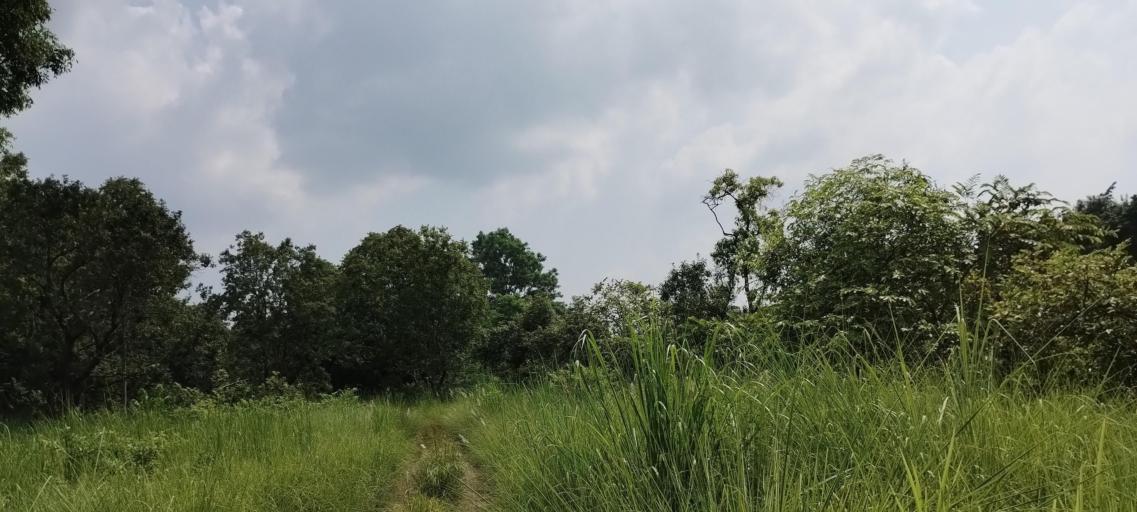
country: NP
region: Far Western
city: Tikapur
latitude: 28.5084
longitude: 81.2477
